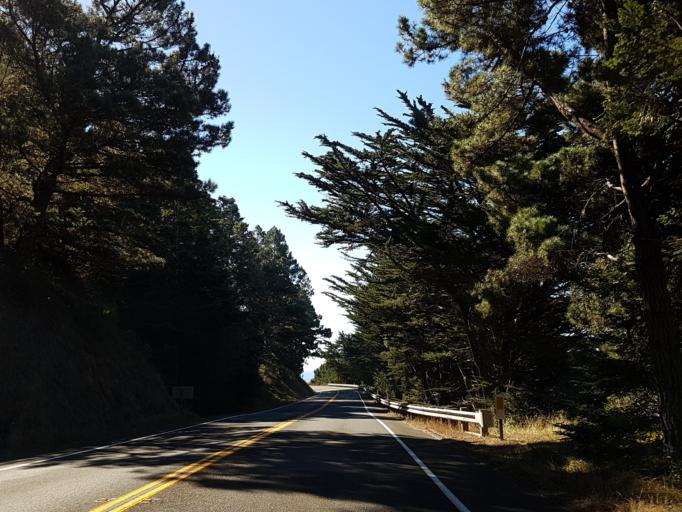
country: US
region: California
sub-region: Mendocino County
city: Fort Bragg
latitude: 39.1867
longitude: -123.7549
